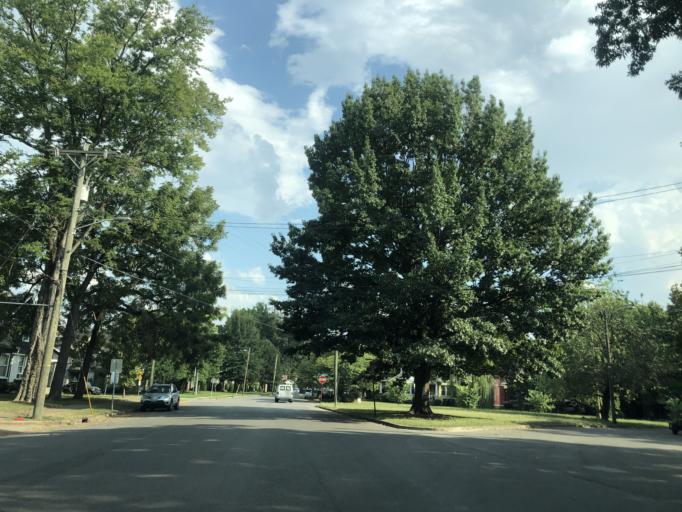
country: US
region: Tennessee
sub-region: Davidson County
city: Nashville
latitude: 36.1316
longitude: -86.7817
